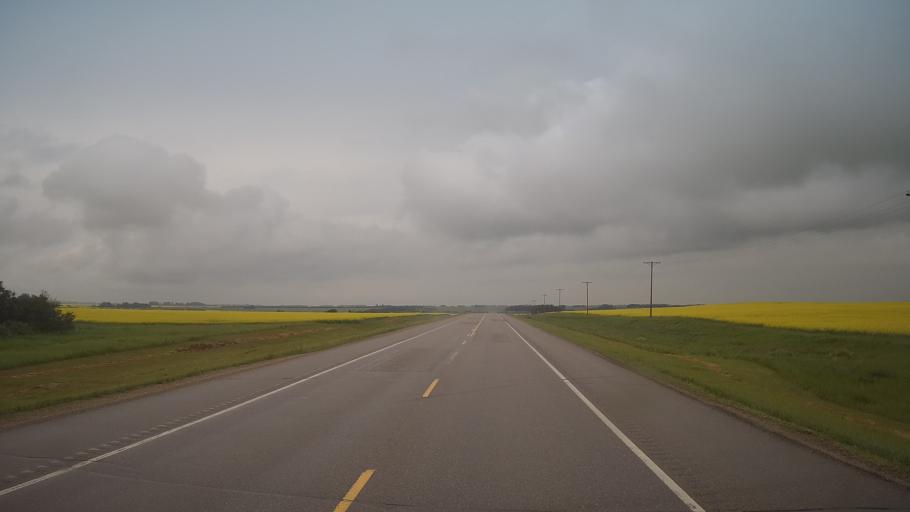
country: CA
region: Saskatchewan
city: Wilkie
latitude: 52.4290
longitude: -108.9158
